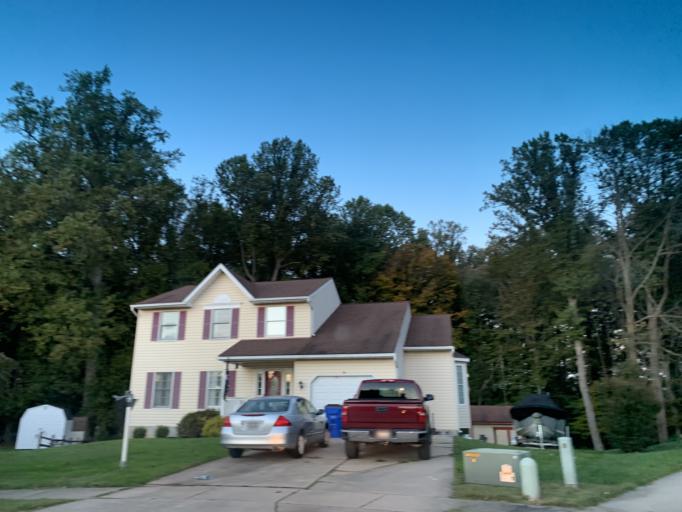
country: US
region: Maryland
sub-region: Harford County
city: South Bel Air
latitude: 39.5463
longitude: -76.3014
